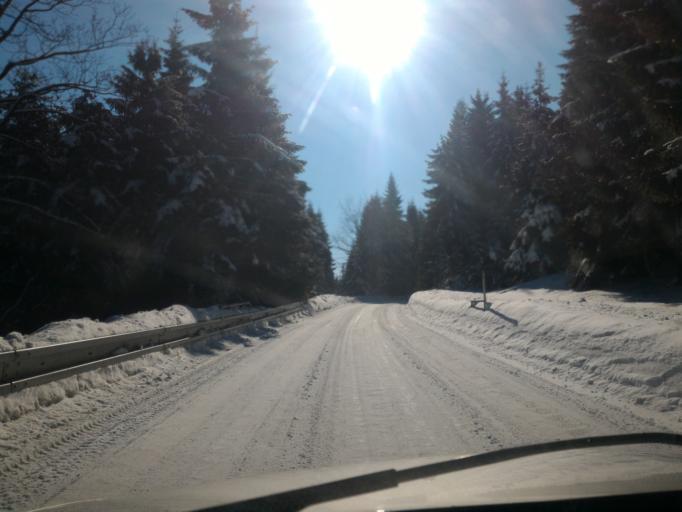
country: CZ
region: Liberecky
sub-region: Okres Jablonec nad Nisou
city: Josefuv Dul
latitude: 50.8488
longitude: 15.2677
